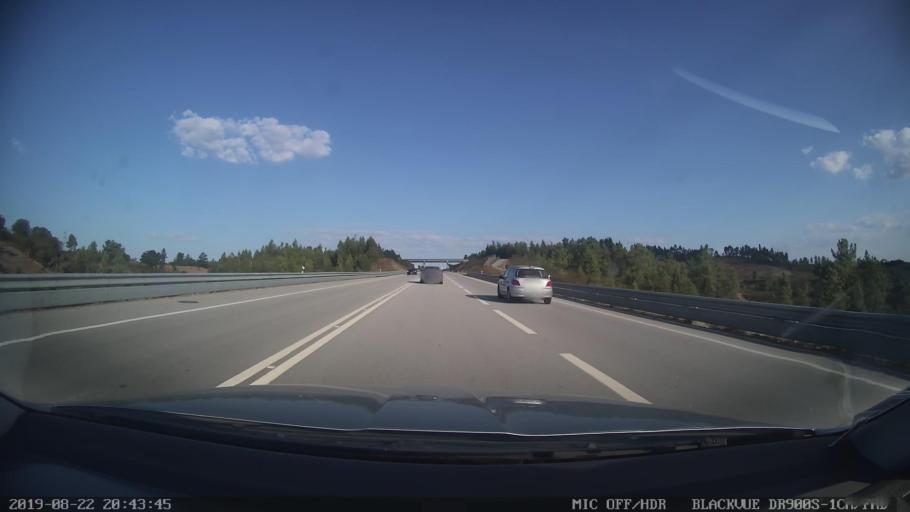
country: PT
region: Castelo Branco
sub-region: Proenca-A-Nova
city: Proenca-a-Nova
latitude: 39.7009
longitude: -7.8381
